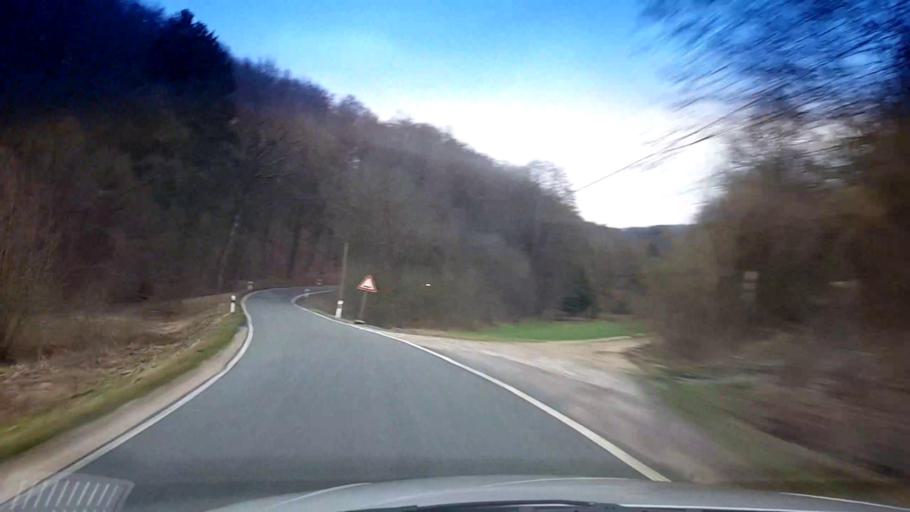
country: DE
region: Bavaria
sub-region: Upper Franconia
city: Wattendorf
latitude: 50.0607
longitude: 11.0602
